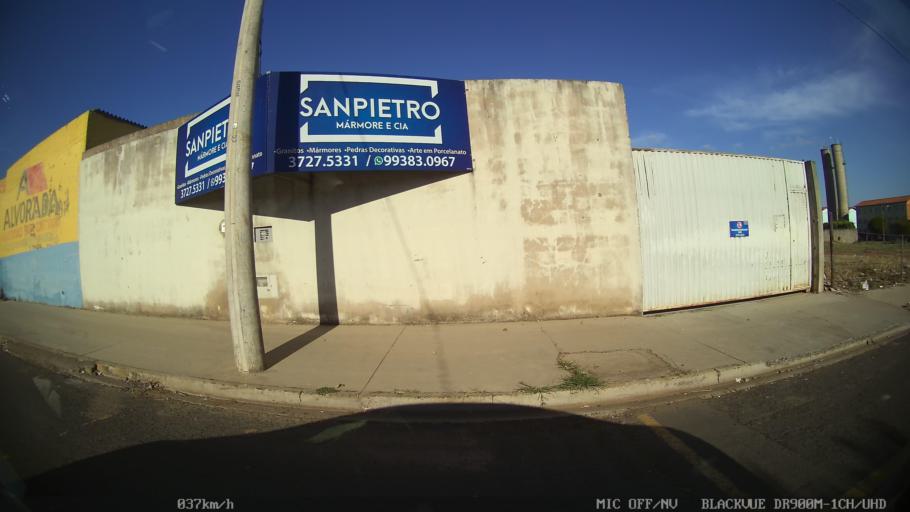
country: BR
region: Sao Paulo
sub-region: Franca
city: Franca
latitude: -20.5056
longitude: -47.4049
